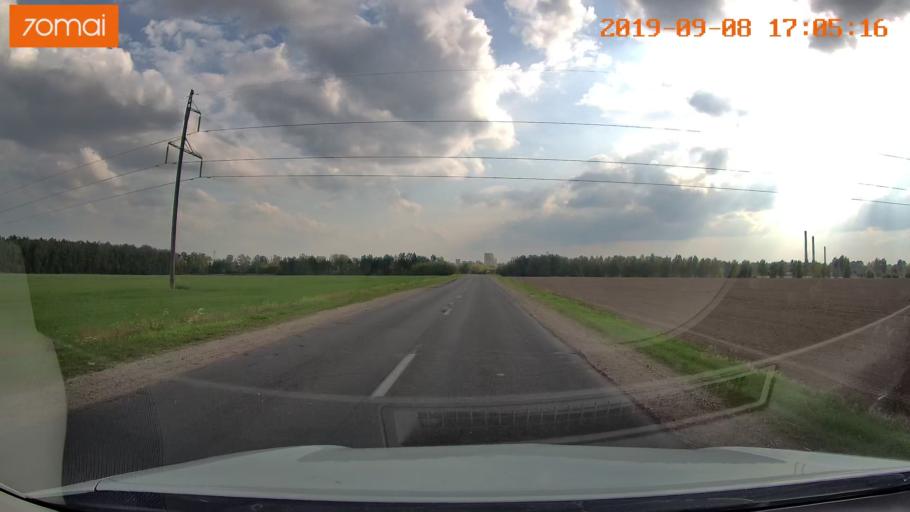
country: BY
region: Grodnenskaya
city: Hrodna
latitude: 53.6798
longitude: 23.9553
